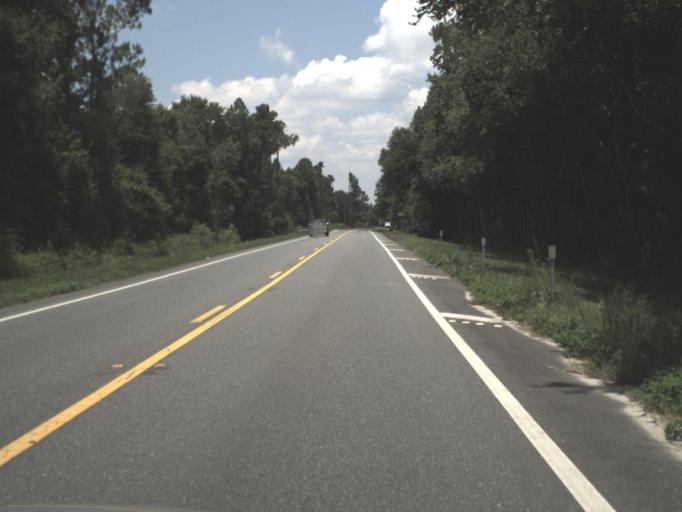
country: US
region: Florida
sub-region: Bradford County
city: Starke
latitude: 30.0238
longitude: -82.1544
